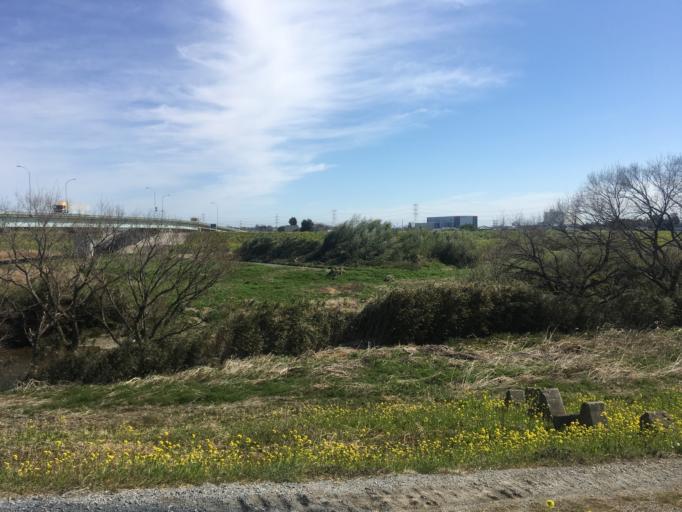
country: JP
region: Saitama
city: Sakado
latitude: 36.0019
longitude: 139.4223
